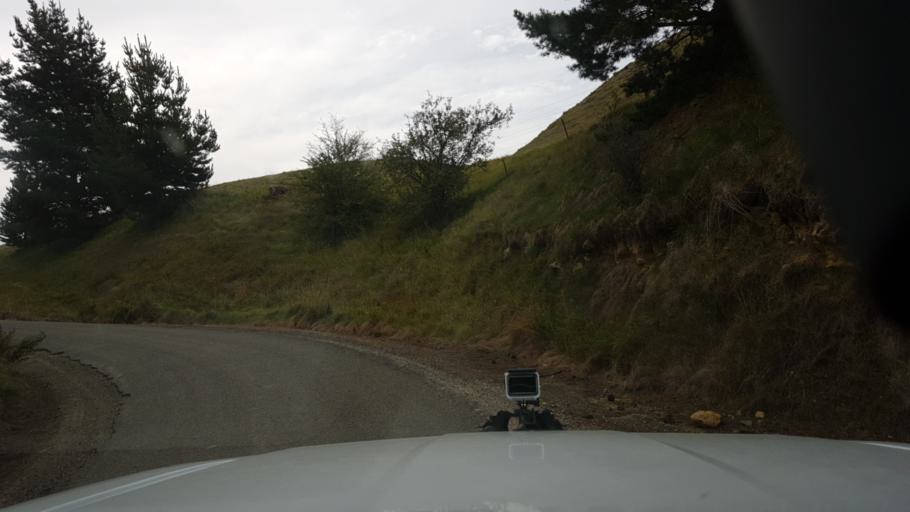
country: NZ
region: Otago
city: Oamaru
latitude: -44.8718
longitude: 170.6409
